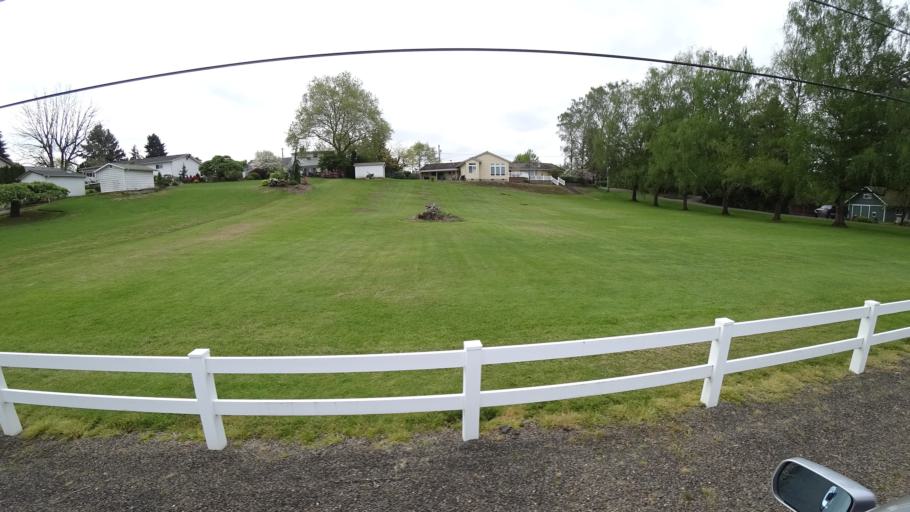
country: US
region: Oregon
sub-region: Washington County
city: Hillsboro
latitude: 45.5291
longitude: -123.0027
